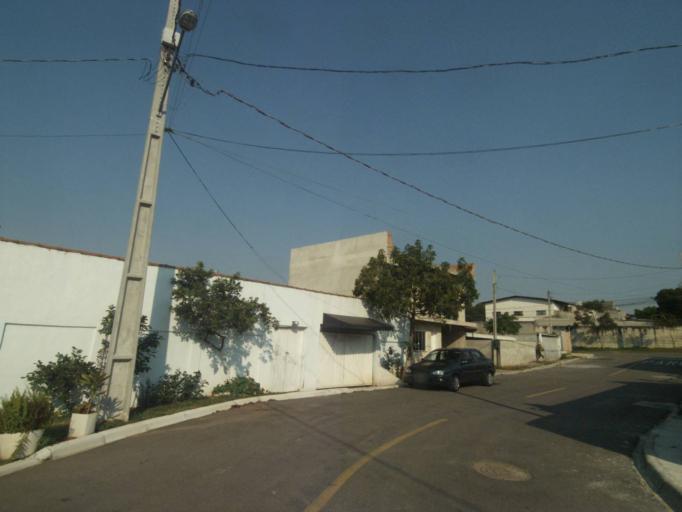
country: BR
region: Parana
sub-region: Curitiba
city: Curitiba
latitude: -25.4915
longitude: -49.2639
